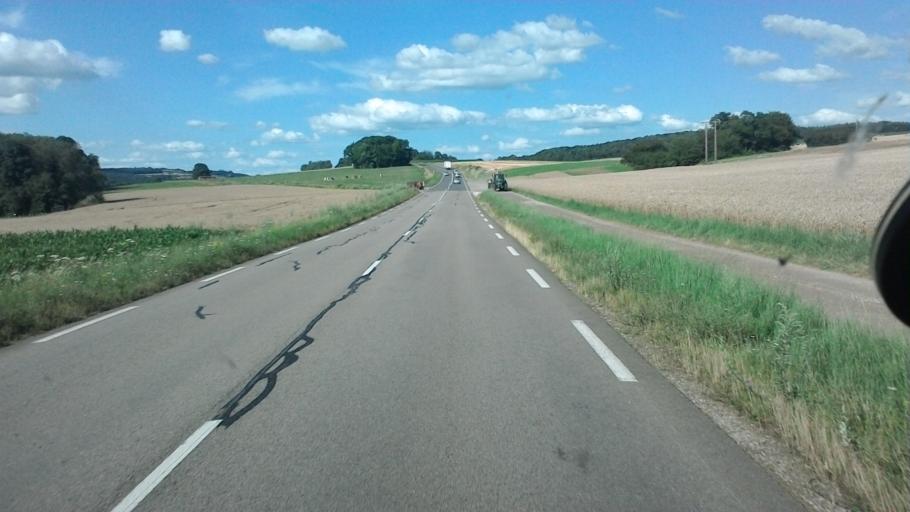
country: FR
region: Franche-Comte
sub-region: Departement de la Haute-Saone
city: Echenoz-la-Meline
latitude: 47.5481
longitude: 6.0590
